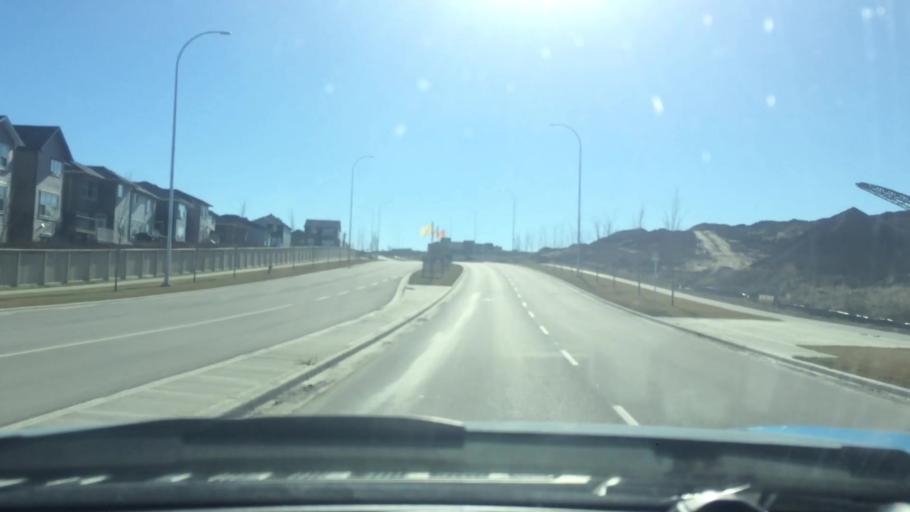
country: CA
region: Alberta
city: Calgary
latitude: 51.1676
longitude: -114.1608
